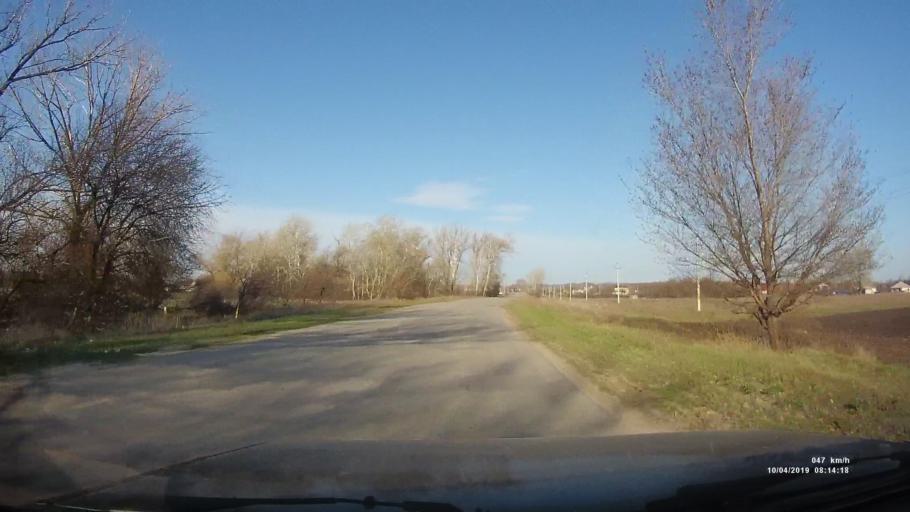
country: RU
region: Rostov
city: Kamensk-Shakhtinskiy
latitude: 48.3603
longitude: 40.2373
